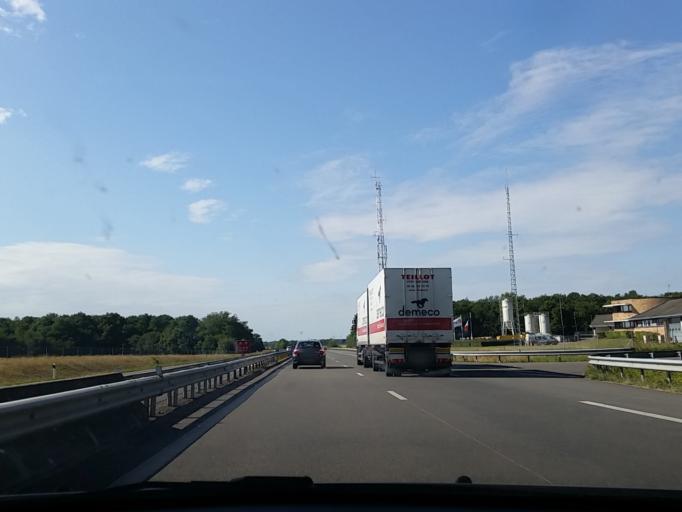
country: FR
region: Centre
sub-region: Departement du Cher
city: Levet
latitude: 46.9186
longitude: 2.4234
